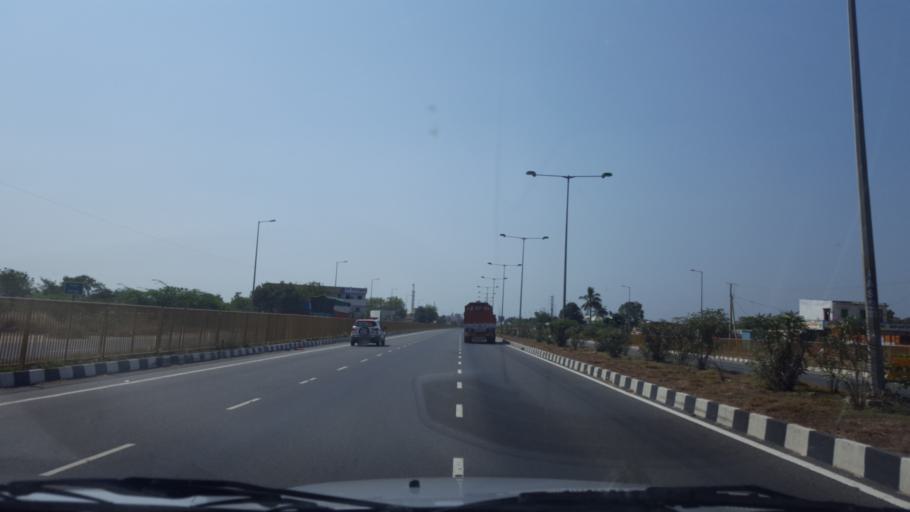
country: IN
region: Andhra Pradesh
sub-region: Guntur
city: Chilakalurupet
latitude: 15.9947
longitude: 80.1084
